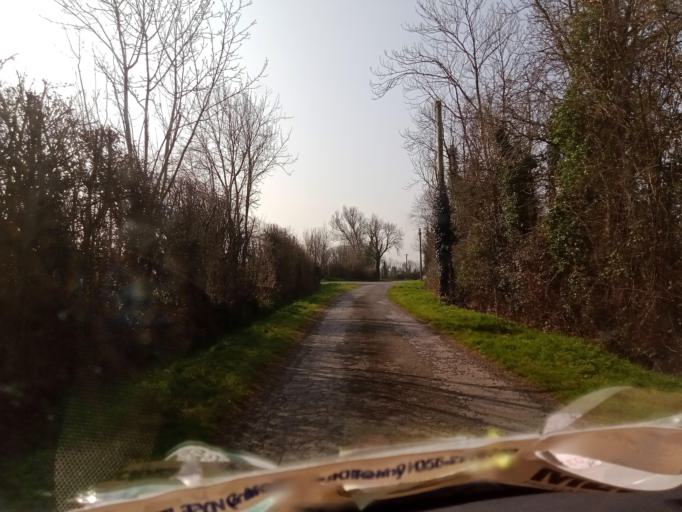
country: IE
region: Leinster
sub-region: Kilkenny
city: Callan
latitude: 52.5237
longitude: -7.4008
